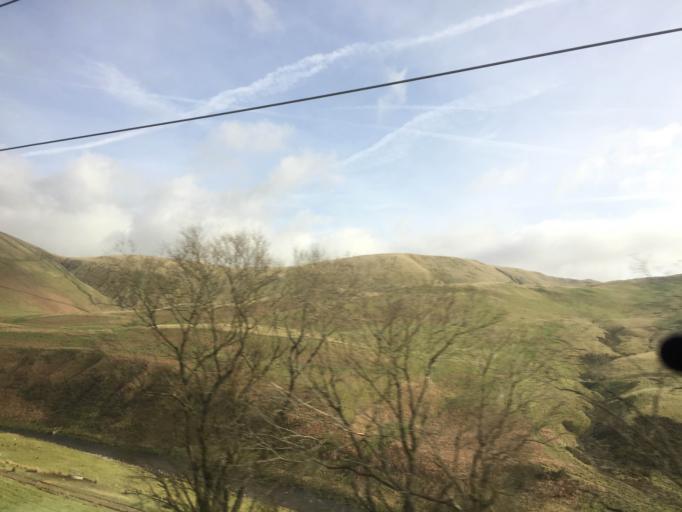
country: GB
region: England
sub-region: Cumbria
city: Sedbergh
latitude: 54.3831
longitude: -2.5812
